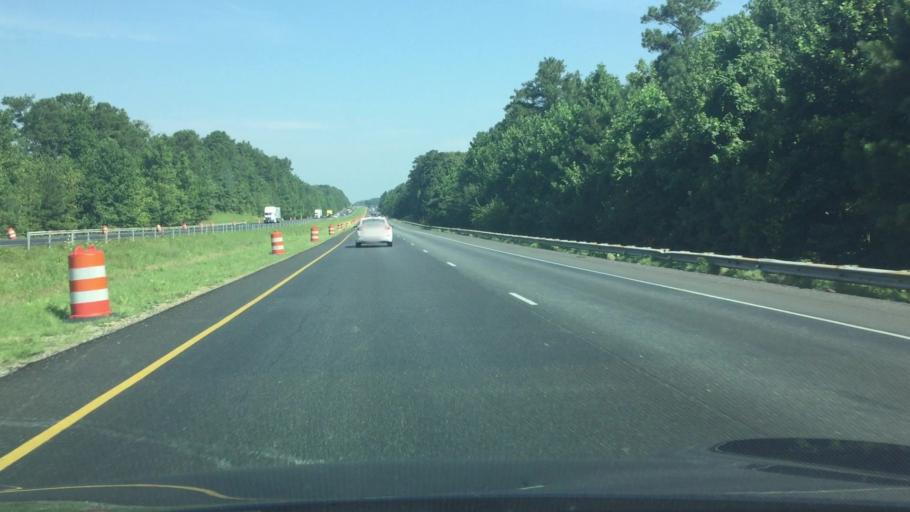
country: US
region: Alabama
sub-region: Autauga County
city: Marbury
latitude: 32.7077
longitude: -86.5249
